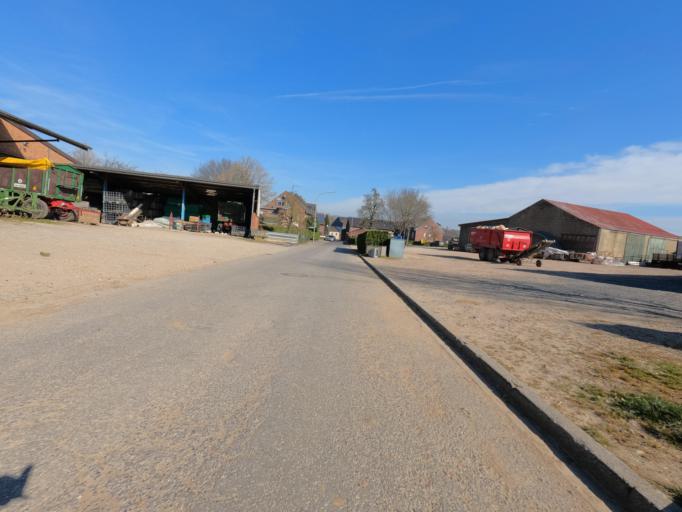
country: DE
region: North Rhine-Westphalia
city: Erkelenz
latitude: 51.0299
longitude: 6.3140
